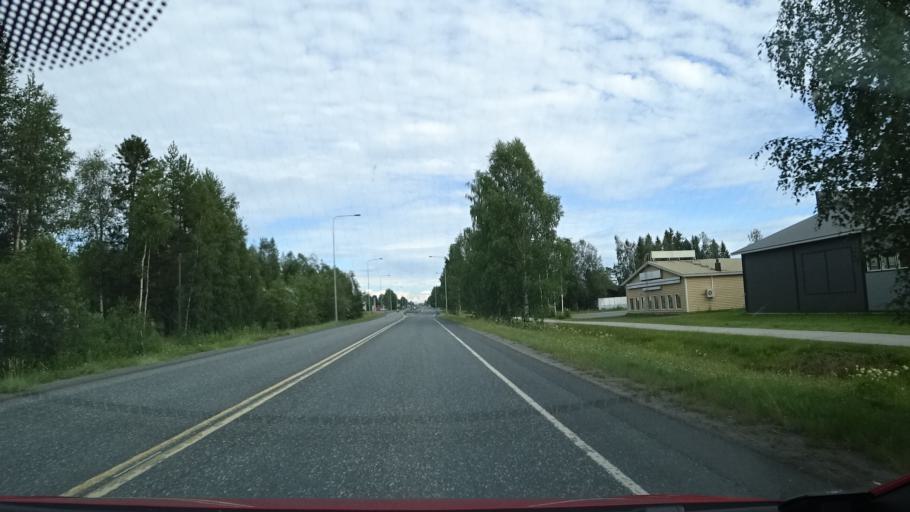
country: FI
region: Lapland
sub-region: Kemi-Tornio
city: Keminmaa
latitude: 65.8013
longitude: 24.4943
